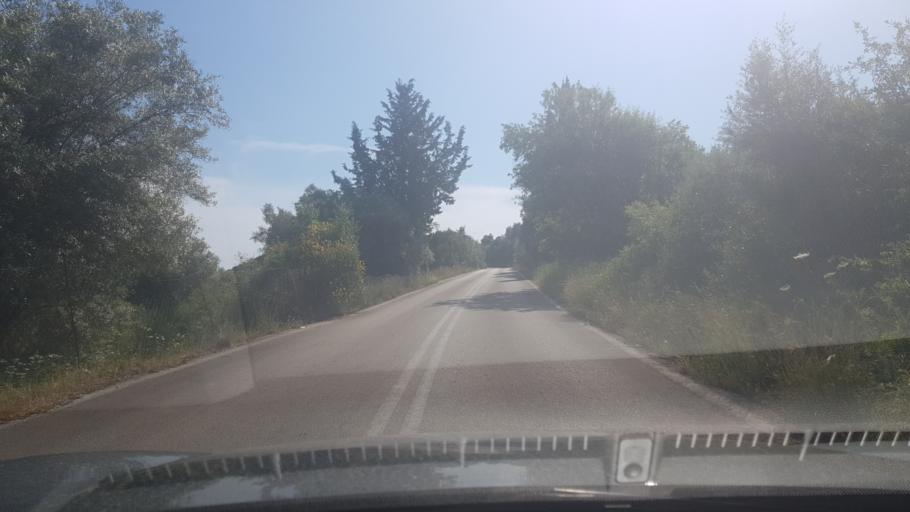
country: GR
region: Ionian Islands
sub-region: Lefkada
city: Nidri
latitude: 38.6540
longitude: 20.6761
